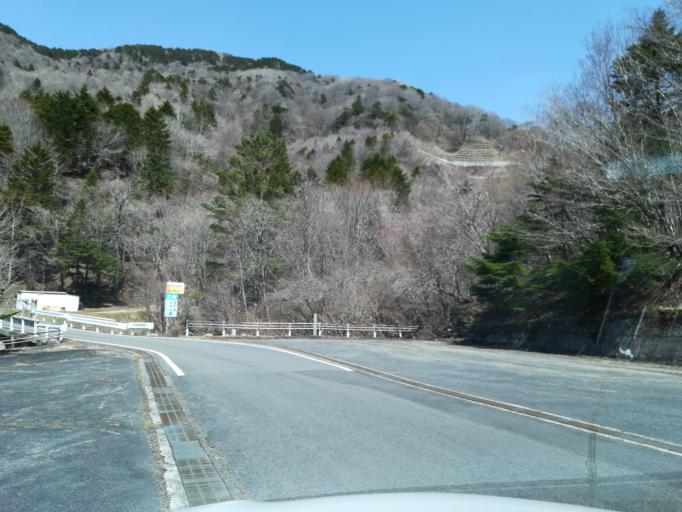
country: JP
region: Tokushima
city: Wakimachi
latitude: 33.8665
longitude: 134.0853
